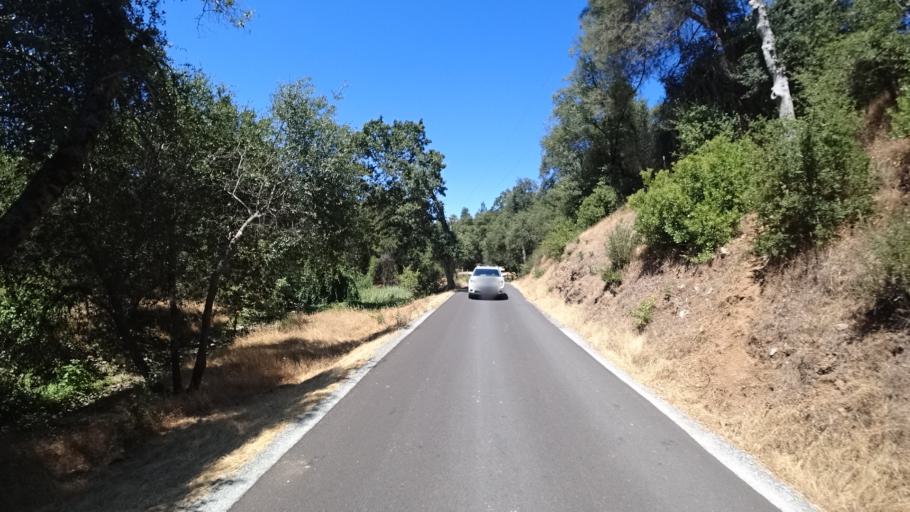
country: US
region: California
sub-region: Calaveras County
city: Murphys
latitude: 38.1297
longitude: -120.4300
